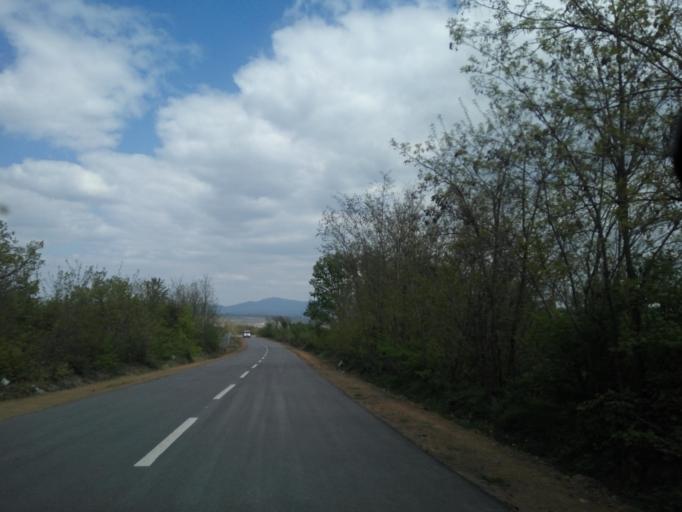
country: XK
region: Gjakova
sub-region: Komuna e Gjakoves
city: Gjakove
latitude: 42.3430
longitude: 20.4701
